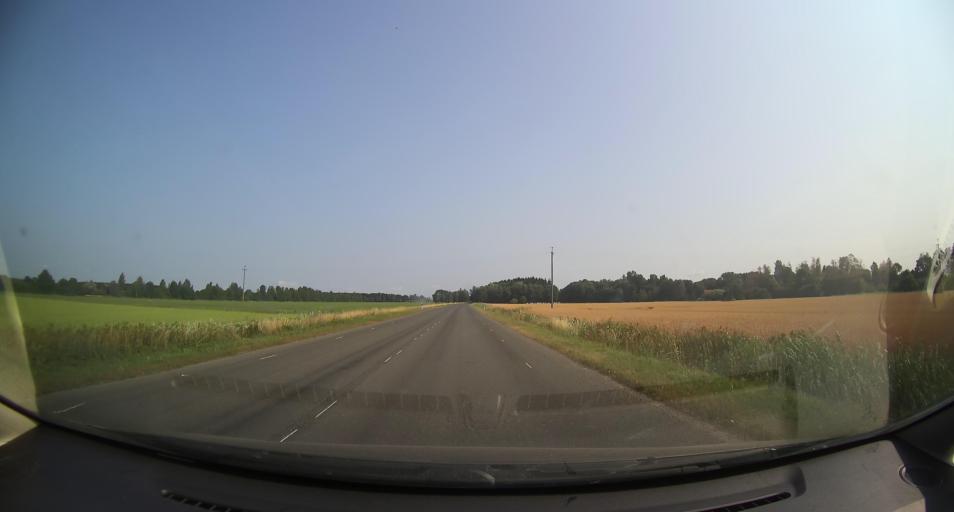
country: EE
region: Paernumaa
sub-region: Audru vald
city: Audru
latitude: 58.4777
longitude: 24.3296
